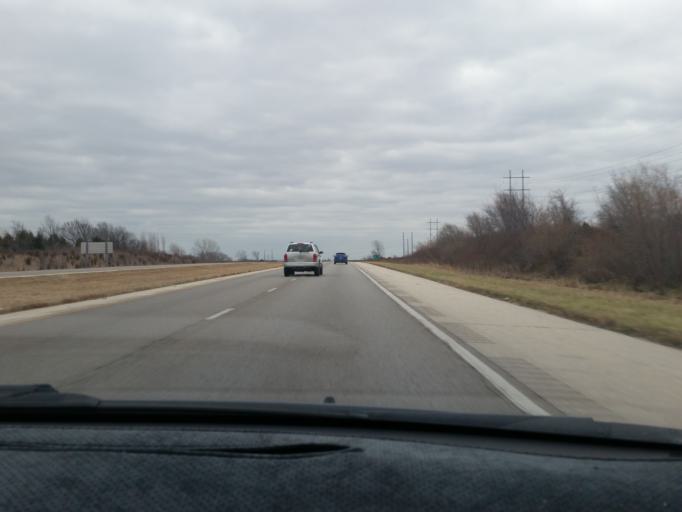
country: US
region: Kansas
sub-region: Johnson County
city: De Soto
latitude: 38.9600
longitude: -94.9445
